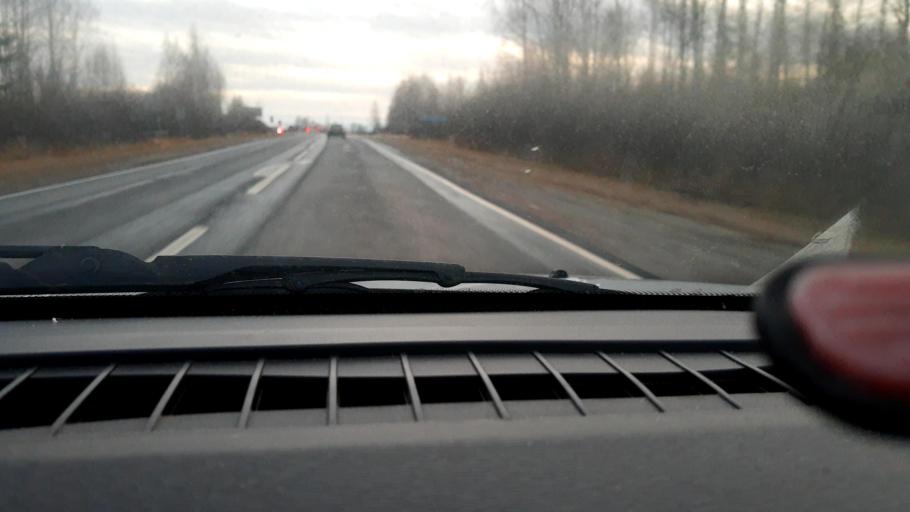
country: RU
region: Nizjnij Novgorod
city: Krasnyye Baki
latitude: 57.0905
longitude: 45.1485
